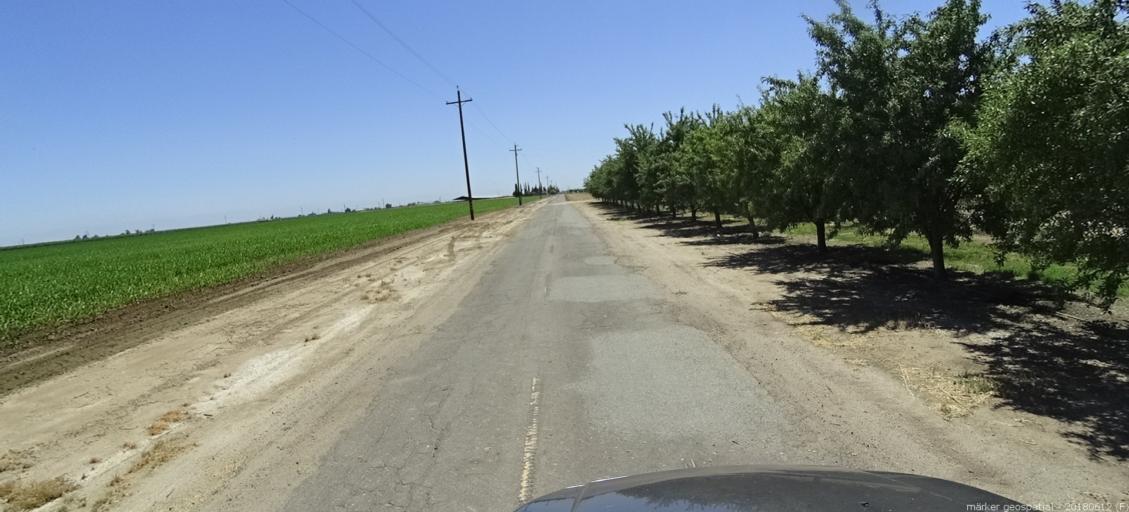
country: US
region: California
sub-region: Madera County
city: Chowchilla
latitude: 37.0616
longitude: -120.3550
